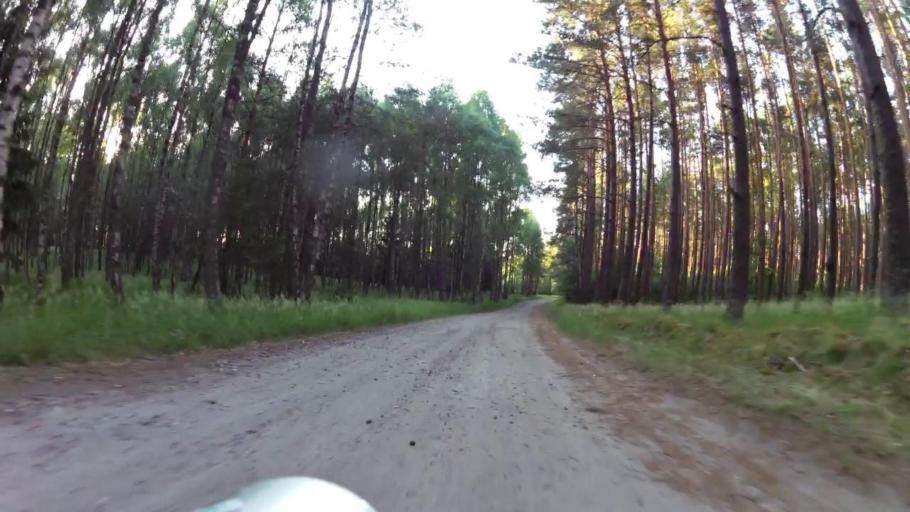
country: PL
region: West Pomeranian Voivodeship
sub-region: Powiat szczecinecki
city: Szczecinek
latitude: 53.8217
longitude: 16.6921
